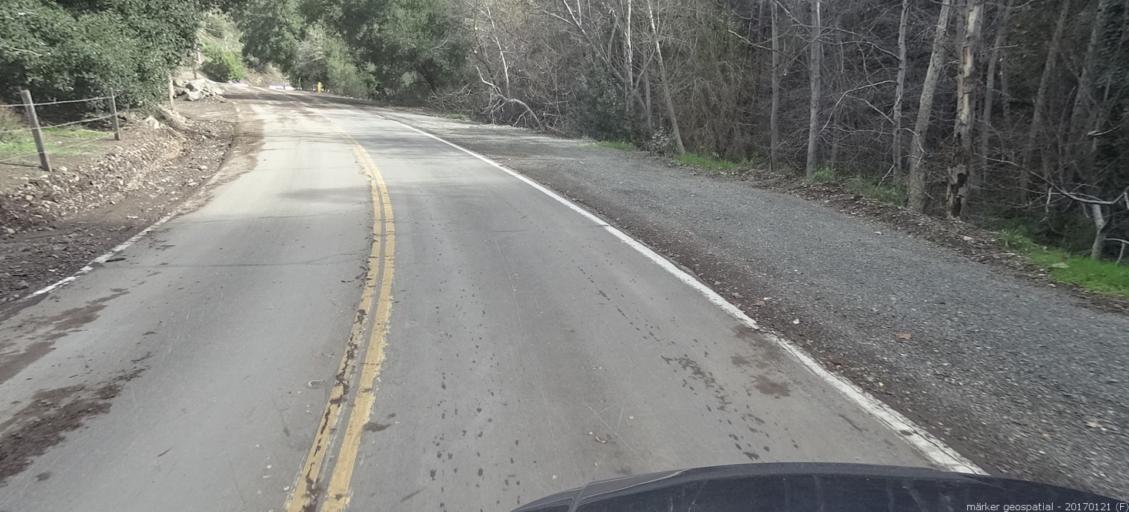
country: US
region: California
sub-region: Orange County
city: Portola Hills
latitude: 33.7458
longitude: -117.6012
